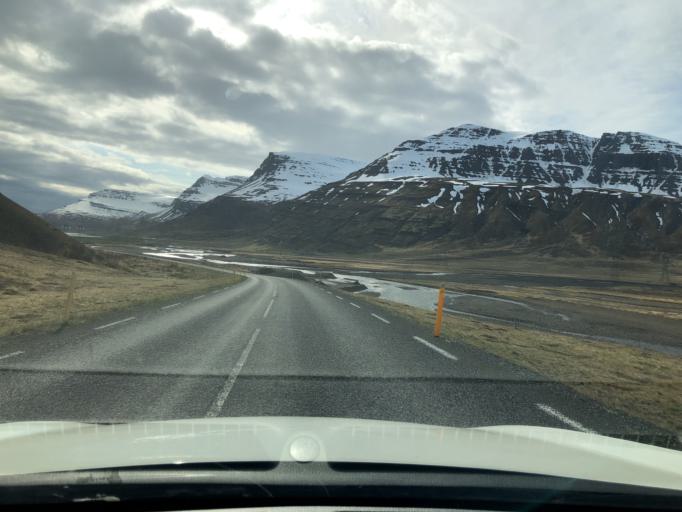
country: IS
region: East
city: Reydarfjoerdur
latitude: 65.0309
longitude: -14.3147
